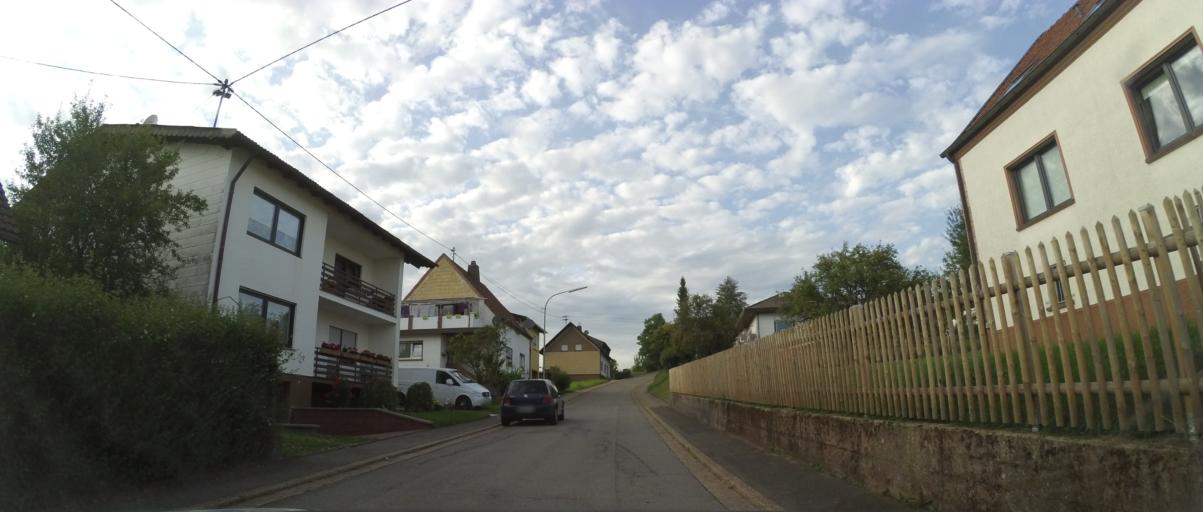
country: DE
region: Saarland
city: Nonnweiler
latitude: 49.5400
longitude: 6.9763
